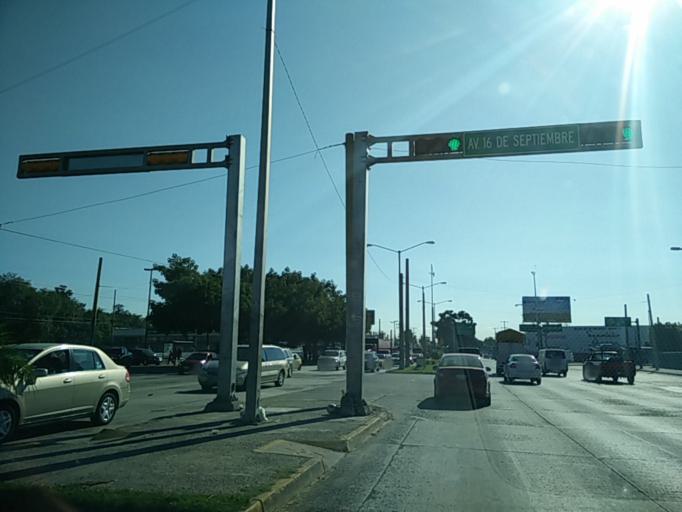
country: MX
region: Jalisco
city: Guadalajara
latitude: 20.6577
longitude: -103.3522
